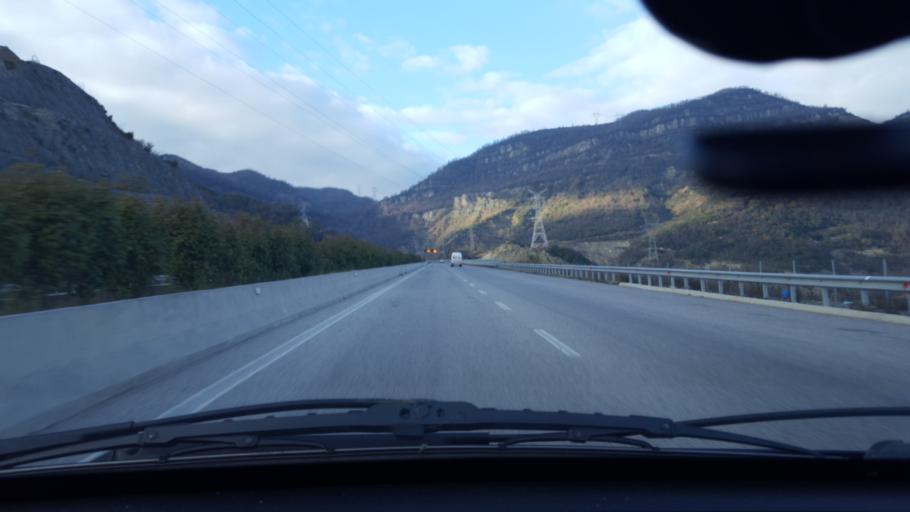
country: AL
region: Tirane
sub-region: Rrethi i Tiranes
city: Krrabe
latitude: 41.1901
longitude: 19.9924
